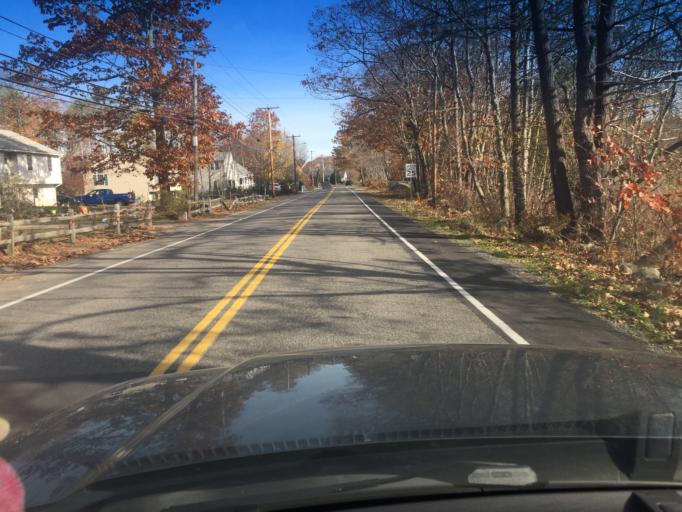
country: US
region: Maine
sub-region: York County
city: York Beach
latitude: 43.1714
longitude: -70.6181
